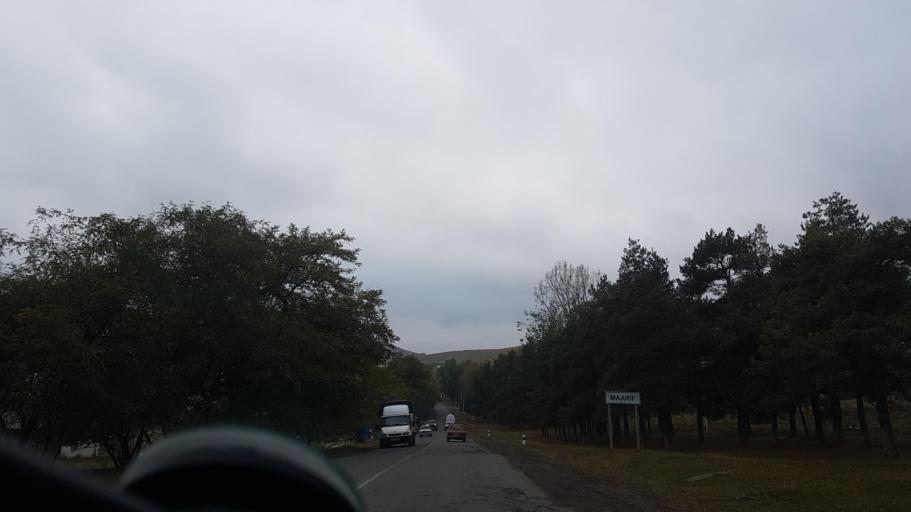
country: AZ
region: Gadabay Rayon
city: Ariqdam
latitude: 40.6381
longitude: 45.8130
